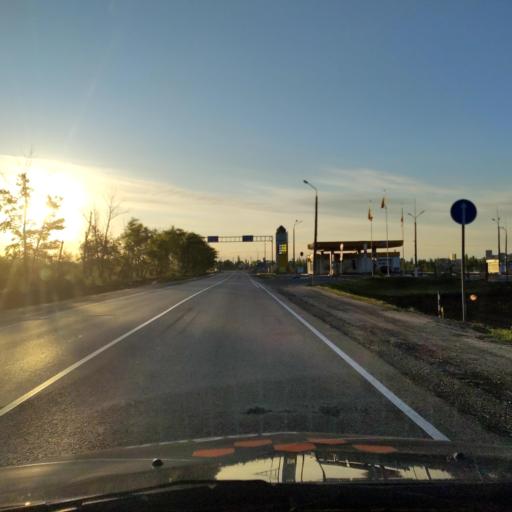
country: RU
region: Orjol
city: Livny
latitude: 52.4410
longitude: 37.5687
